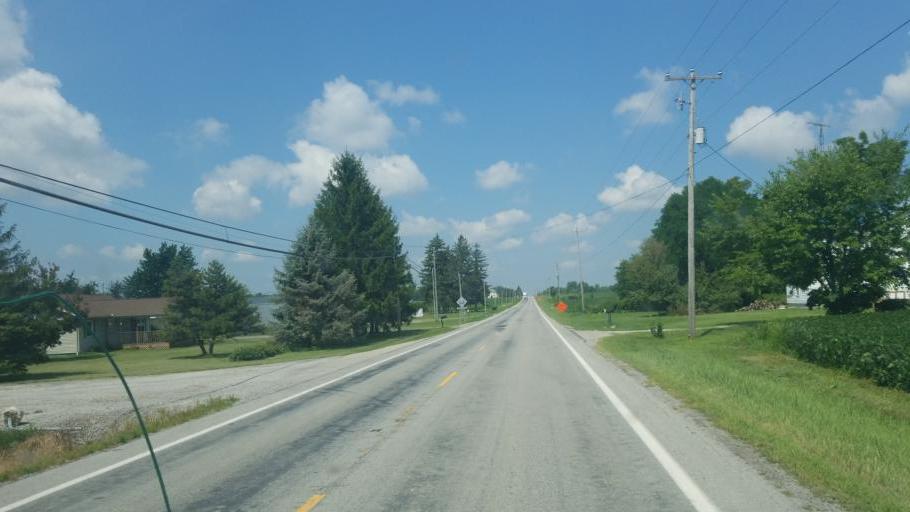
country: US
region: Ohio
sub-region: Allen County
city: Lima
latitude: 40.7155
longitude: -84.0287
